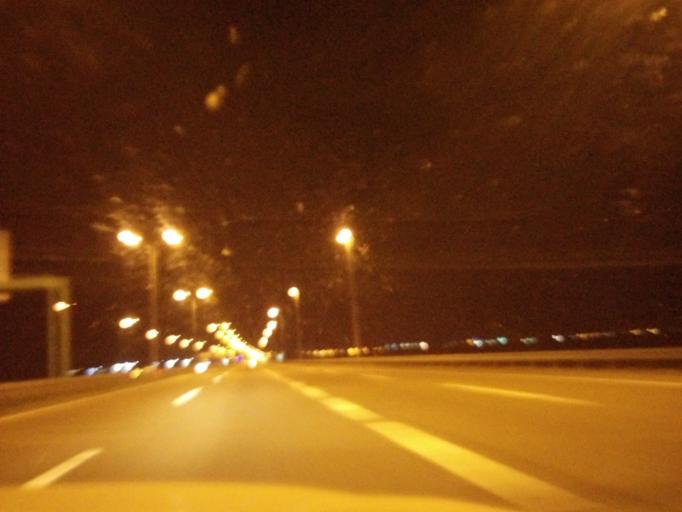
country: RS
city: Dobanovci
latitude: 44.8395
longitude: 20.2313
